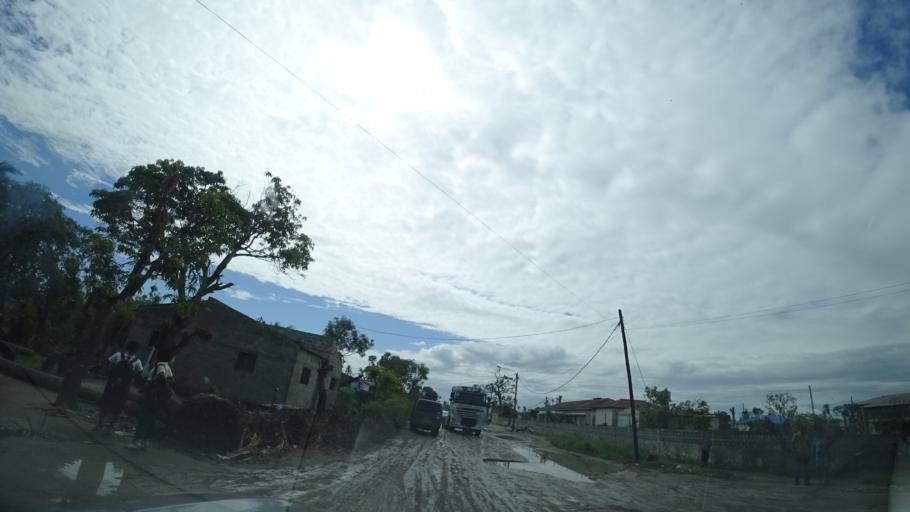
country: MZ
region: Sofala
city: Beira
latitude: -19.7685
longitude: 34.8681
